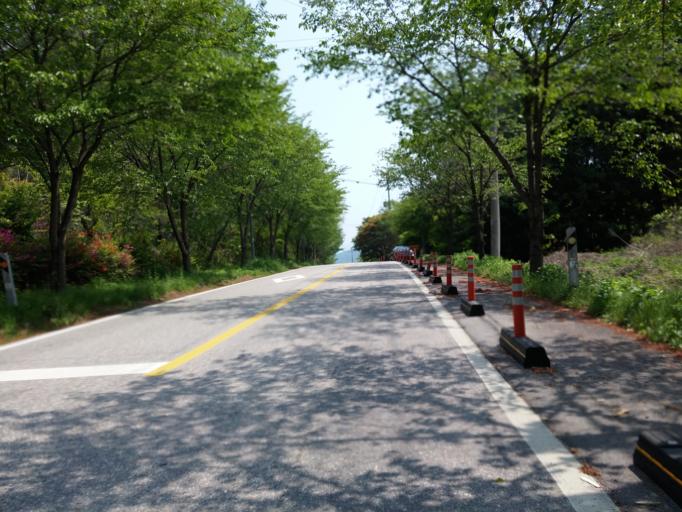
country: KR
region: Daejeon
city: Sintansin
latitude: 36.4302
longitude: 127.5394
